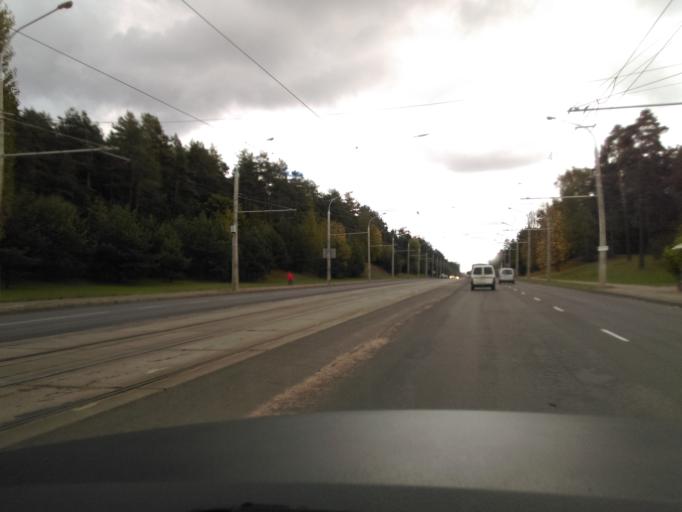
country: BY
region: Minsk
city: Minsk
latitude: 53.8843
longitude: 27.6207
